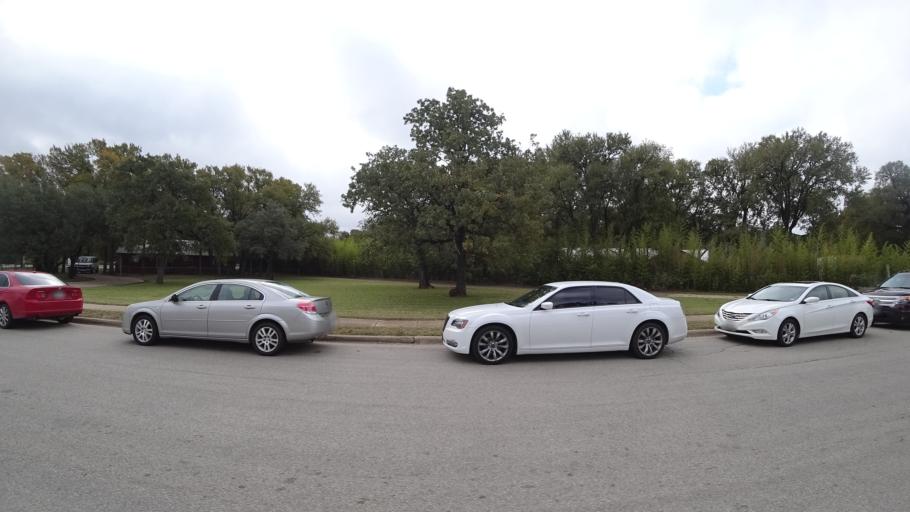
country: US
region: Texas
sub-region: Travis County
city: Shady Hollow
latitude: 30.2116
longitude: -97.8329
